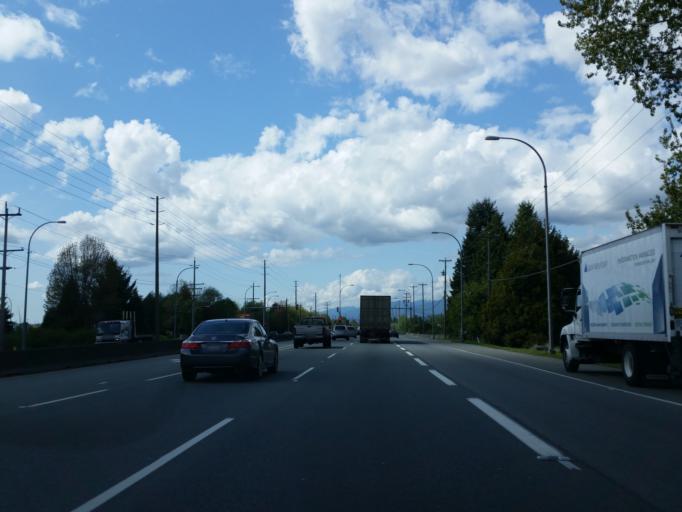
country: CA
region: British Columbia
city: Pitt Meadows
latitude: 49.2345
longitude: -122.6981
